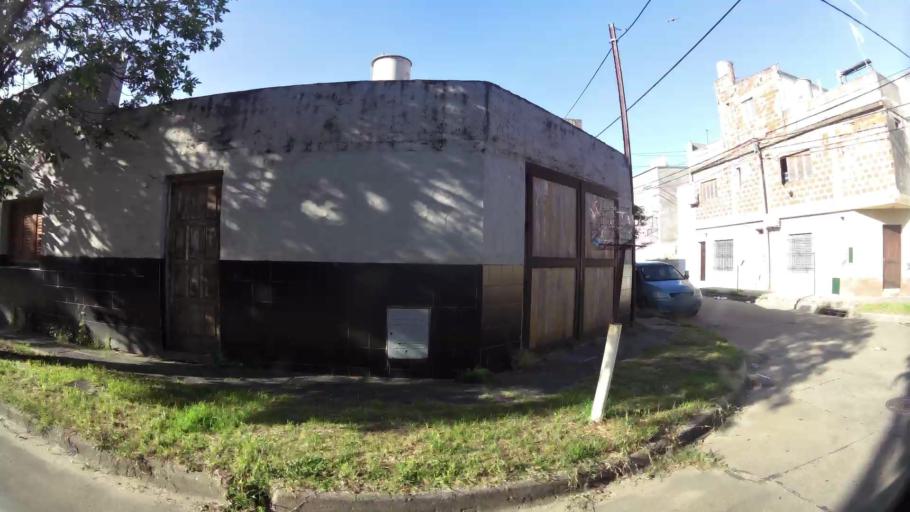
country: AR
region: Santa Fe
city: Santa Fe de la Vera Cruz
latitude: -31.6117
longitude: -60.6973
